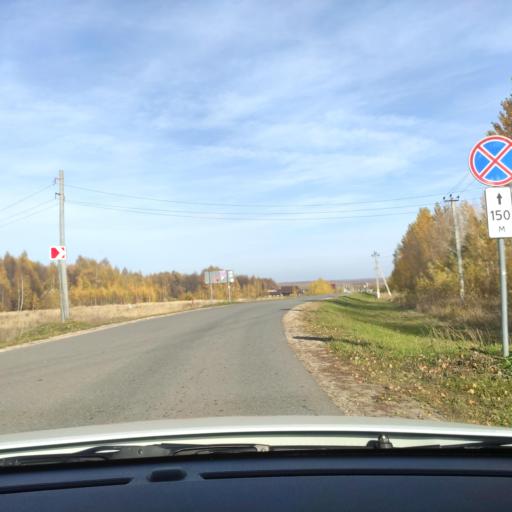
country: RU
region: Tatarstan
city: Pestretsy
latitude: 55.7259
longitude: 49.4573
